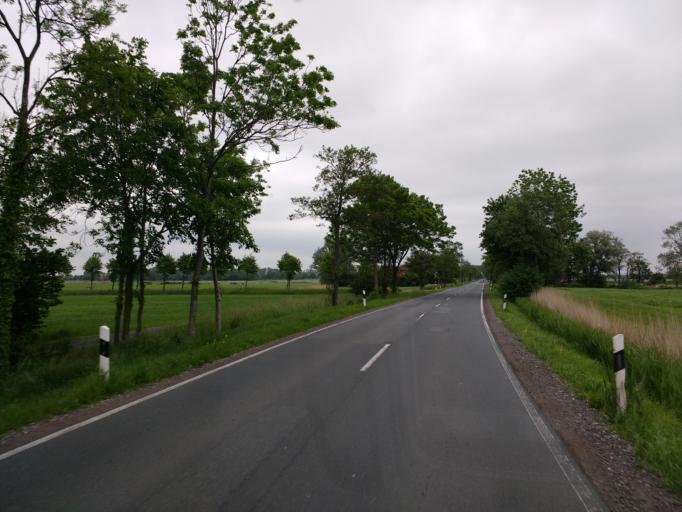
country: DE
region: Lower Saxony
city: Jever
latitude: 53.5949
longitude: 7.9181
